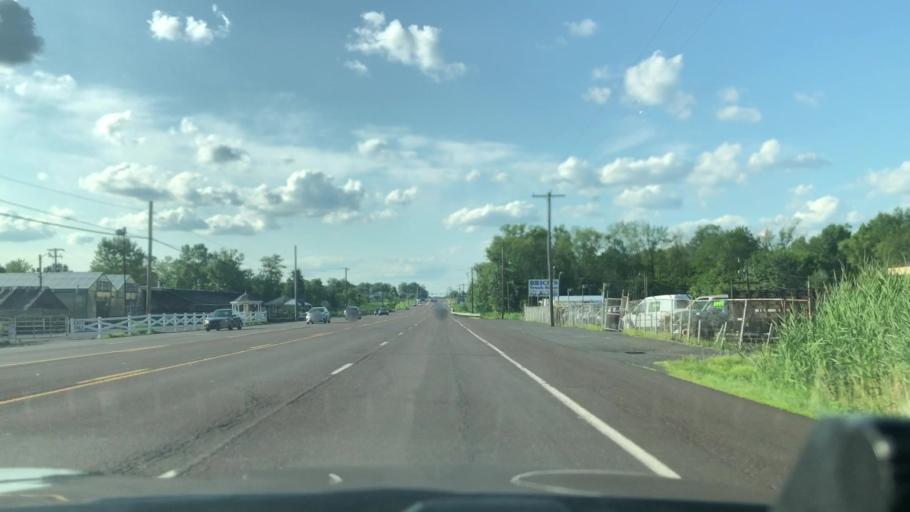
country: US
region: Pennsylvania
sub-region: Bucks County
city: Quakertown
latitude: 40.4113
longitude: -75.3408
